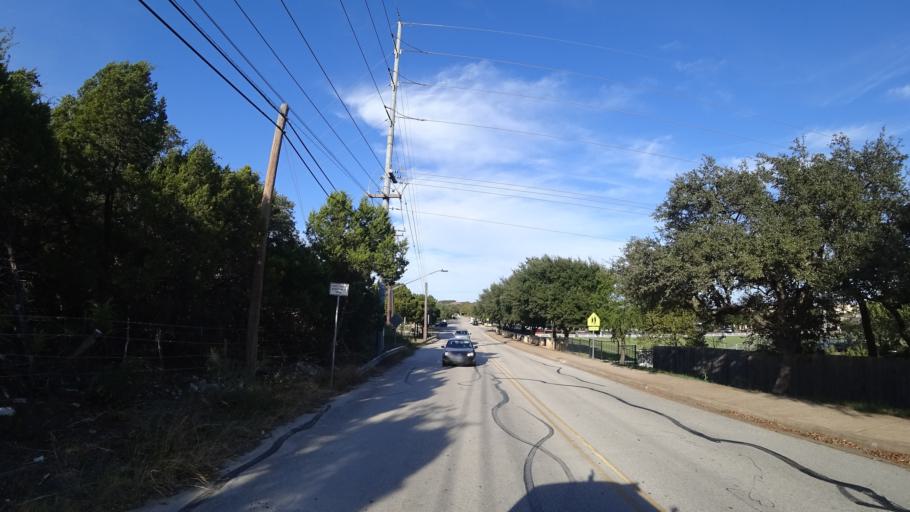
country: US
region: Texas
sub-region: Travis County
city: Barton Creek
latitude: 30.2536
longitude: -97.8461
